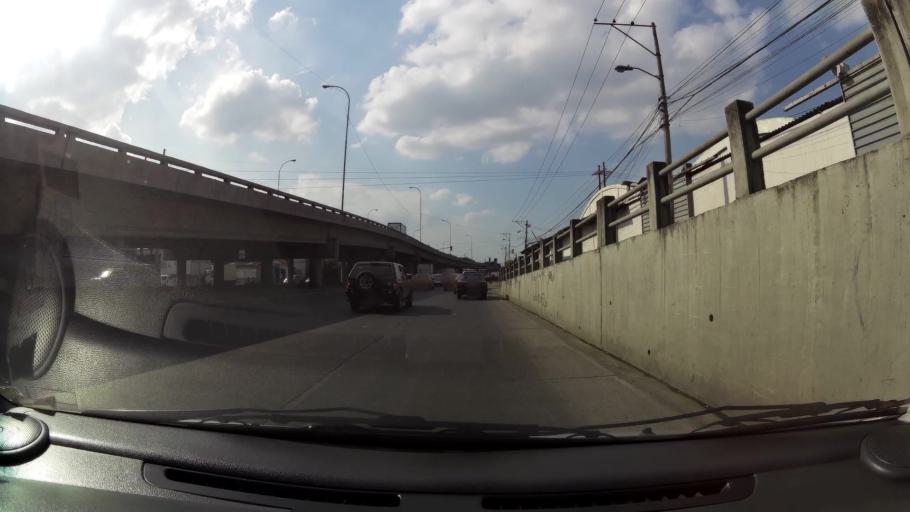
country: EC
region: Guayas
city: Guayaquil
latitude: -2.1313
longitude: -79.9331
